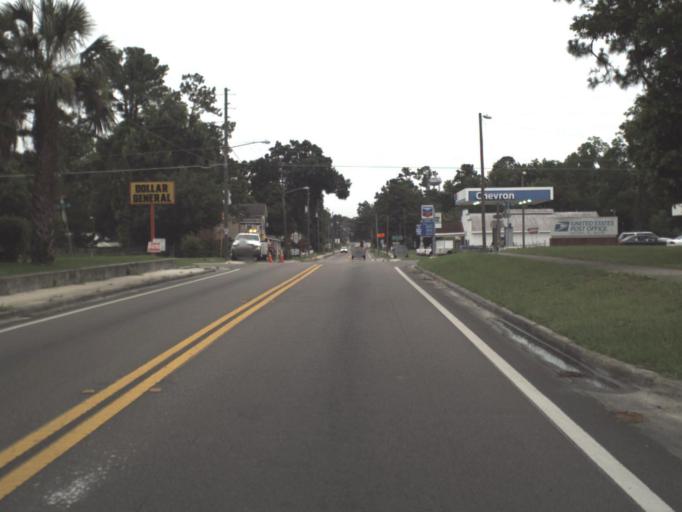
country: US
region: Florida
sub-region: Alachua County
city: Archer
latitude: 29.5296
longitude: -82.5191
